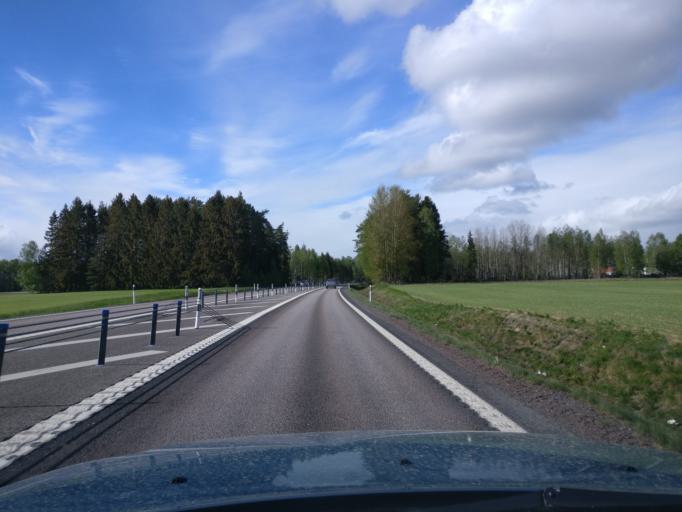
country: SE
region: Vaermland
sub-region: Forshaga Kommun
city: Forshaga
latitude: 59.4709
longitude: 13.4120
